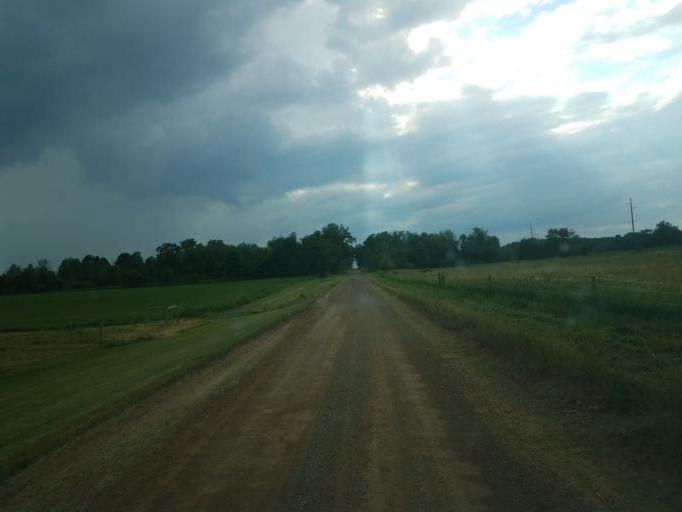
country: US
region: Michigan
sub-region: Barry County
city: Nashville
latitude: 42.5968
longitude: -84.9978
